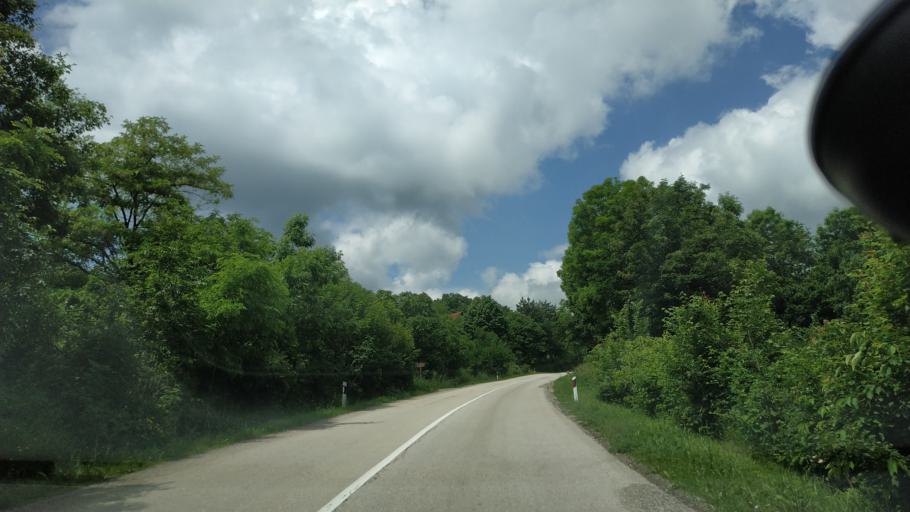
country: RS
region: Central Serbia
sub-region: Borski Okrug
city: Bor
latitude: 44.0835
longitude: 22.0107
